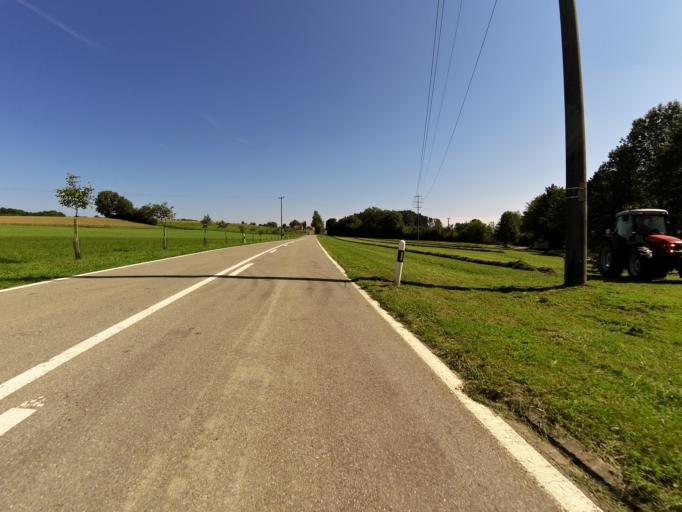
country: CH
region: Thurgau
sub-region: Weinfelden District
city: Maerstetten-Dorf
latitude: 47.6038
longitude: 9.0779
